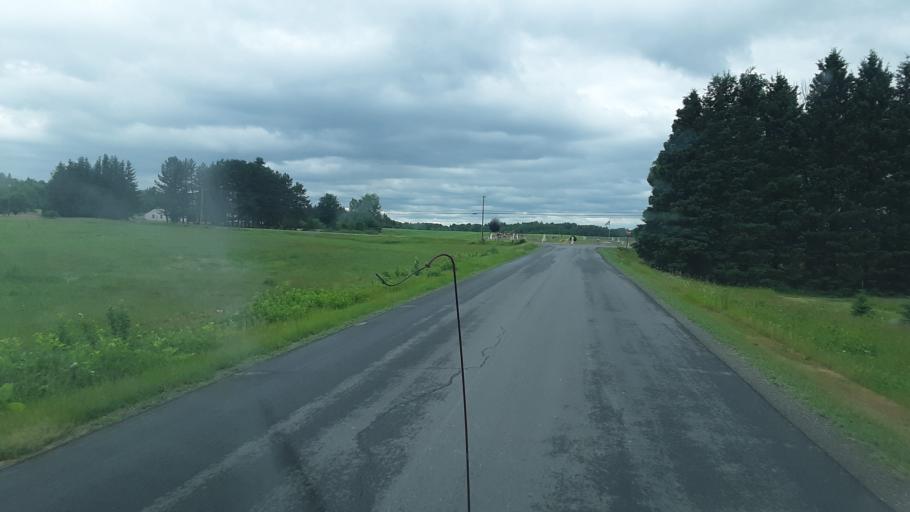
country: US
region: Maine
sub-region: Aroostook County
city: Presque Isle
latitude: 46.7323
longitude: -68.1801
